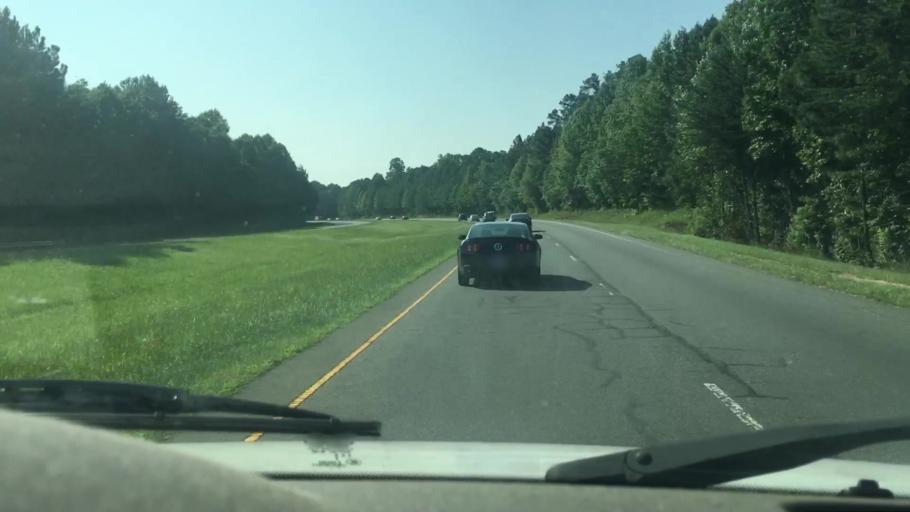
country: US
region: North Carolina
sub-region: Gaston County
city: Mount Holly
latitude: 35.3425
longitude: -80.9671
